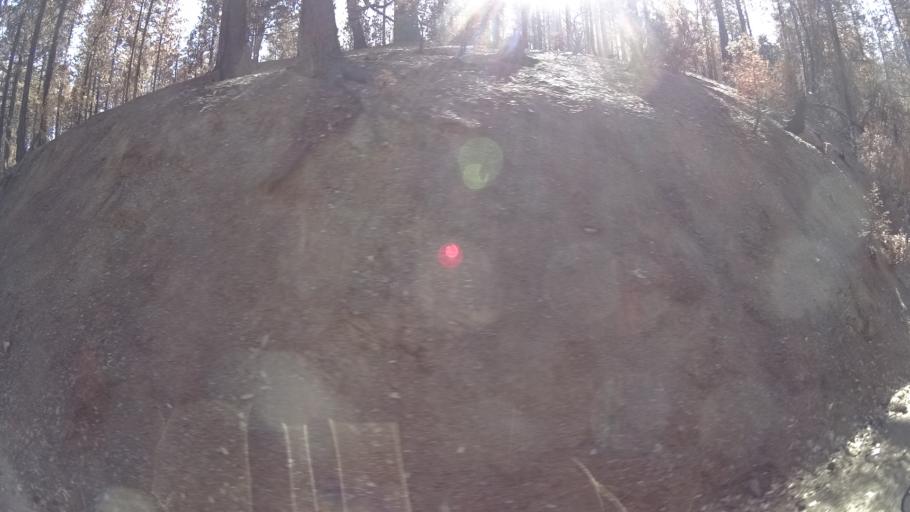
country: US
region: California
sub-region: Tehama County
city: Rancho Tehama Reserve
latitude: 39.6618
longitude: -122.7146
